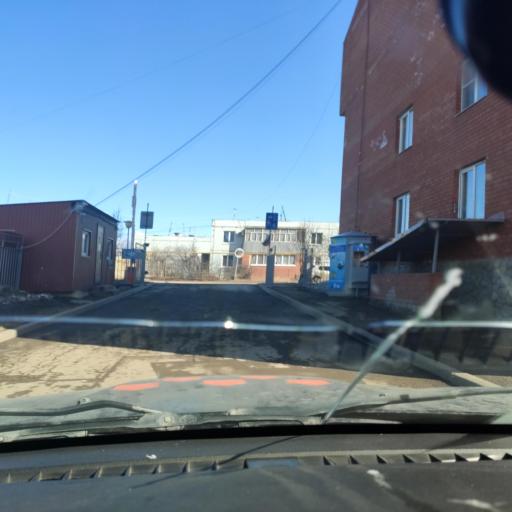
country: RU
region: Samara
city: Podstepki
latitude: 53.5138
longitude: 49.1136
